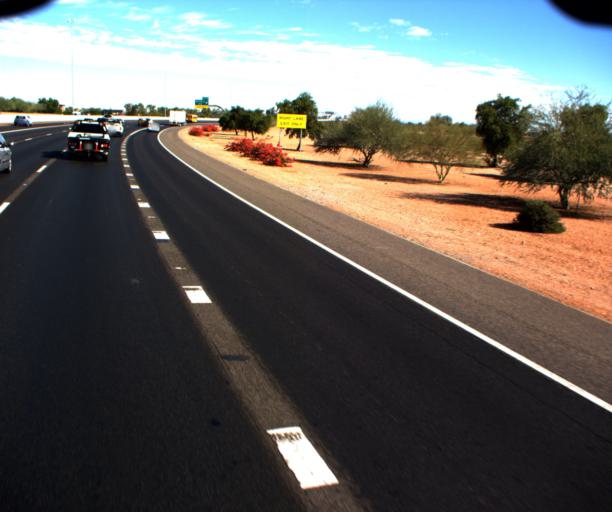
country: US
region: Arizona
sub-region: Maricopa County
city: Peoria
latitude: 33.5451
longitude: -112.2714
